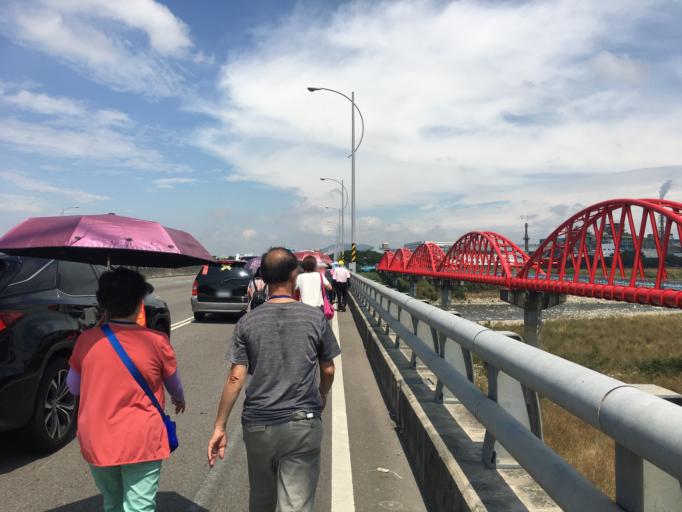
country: TW
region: Taiwan
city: Fengyuan
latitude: 24.2792
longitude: 120.7225
